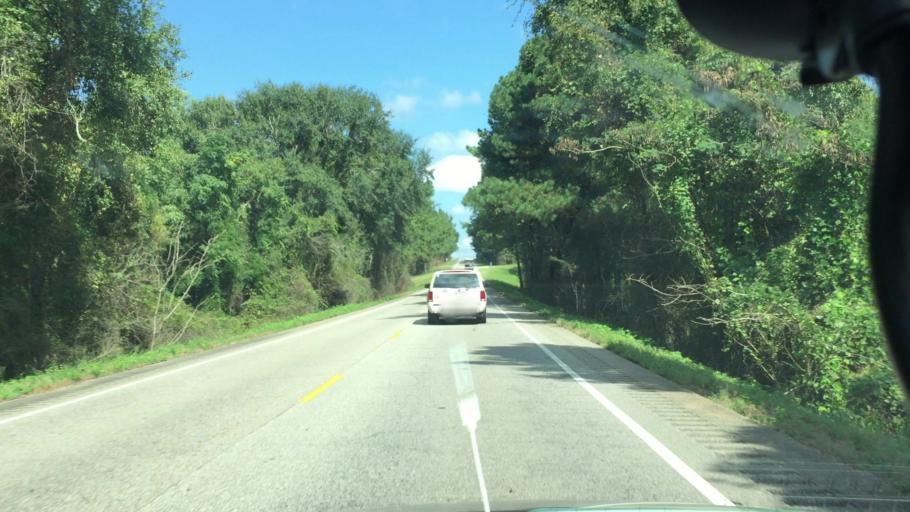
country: US
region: Alabama
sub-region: Coffee County
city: New Brockton
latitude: 31.4045
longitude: -85.8817
